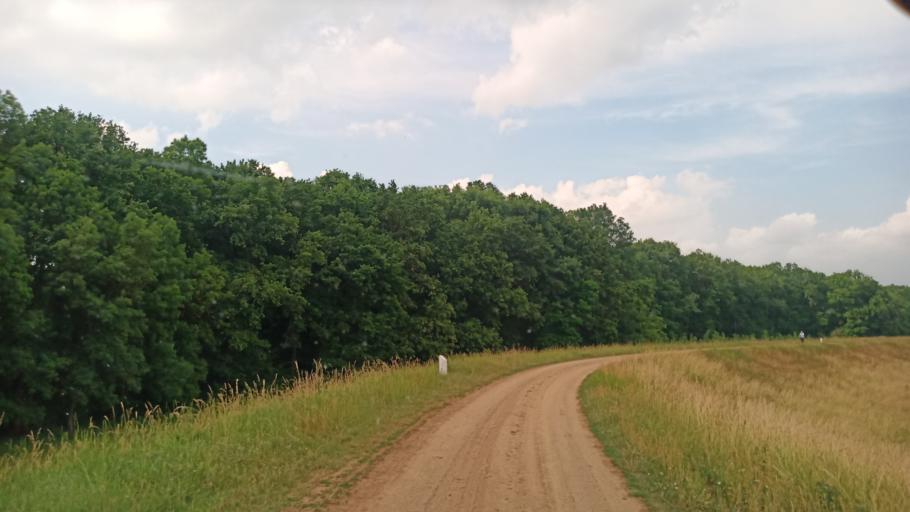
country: HU
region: Bekes
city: Doboz
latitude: 46.7044
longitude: 21.2773
